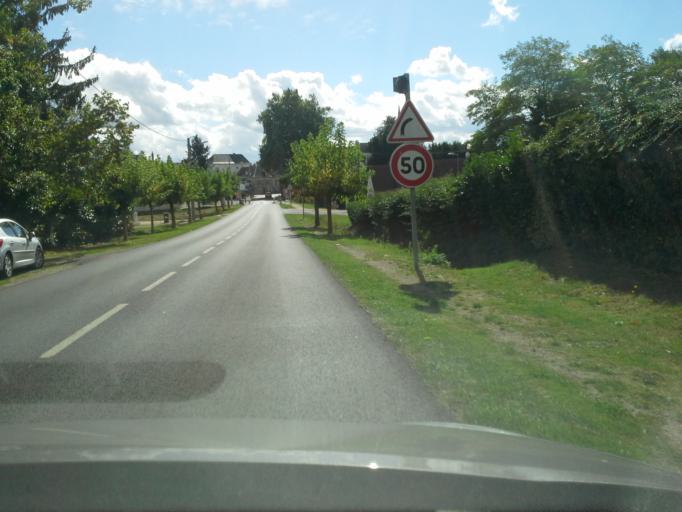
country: FR
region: Centre
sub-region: Departement du Loir-et-Cher
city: Les Montils
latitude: 47.4404
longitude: 1.2960
